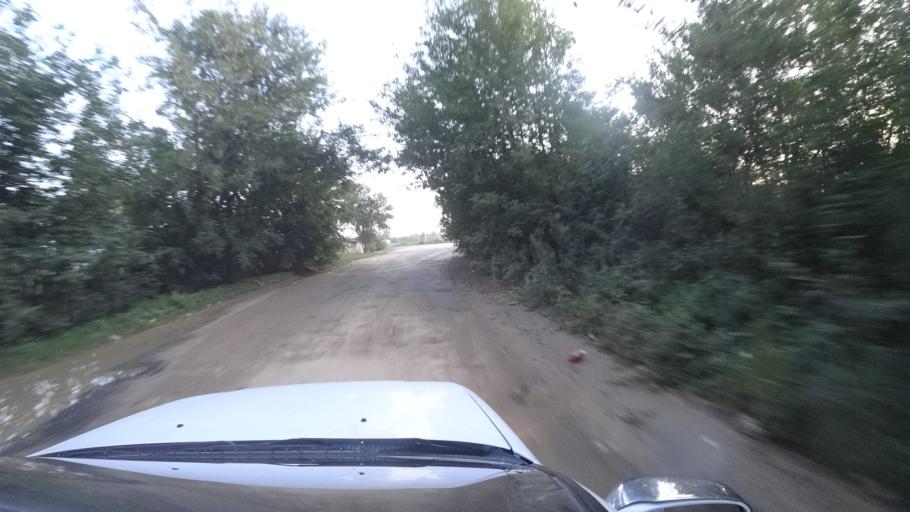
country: RU
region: Primorskiy
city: Dal'nerechensk
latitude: 45.9326
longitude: 133.7582
